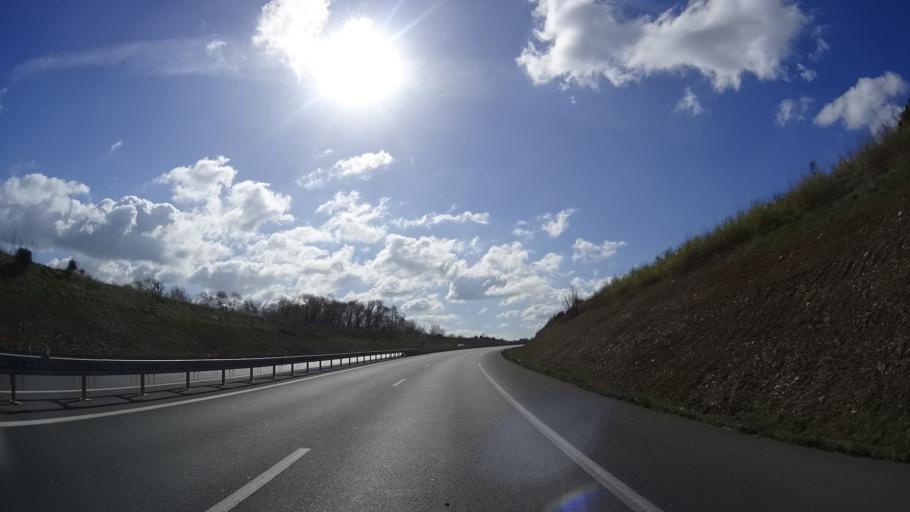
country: FR
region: Pays de la Loire
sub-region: Departement de Maine-et-Loire
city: Saint-Melaine-sur-Aubance
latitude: 47.3962
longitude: -0.5047
